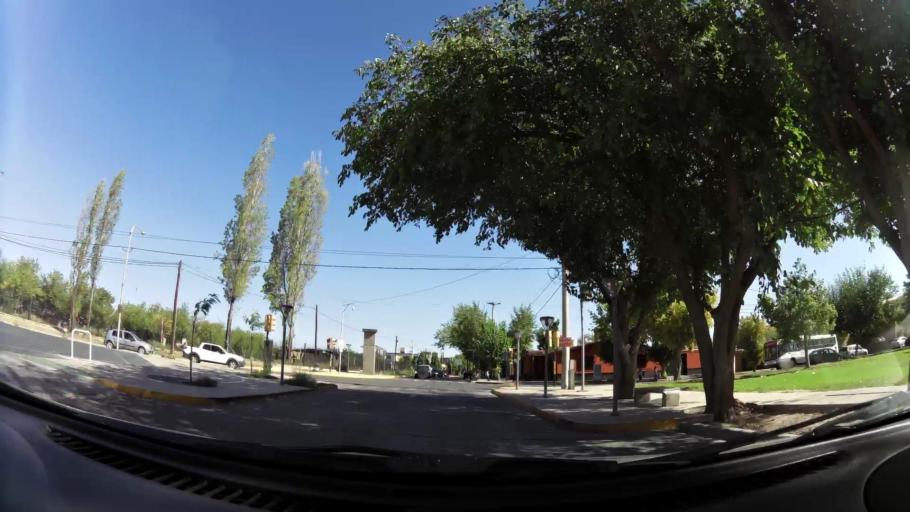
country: AR
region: Mendoza
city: Villa Nueva
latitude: -32.9129
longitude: -68.7976
